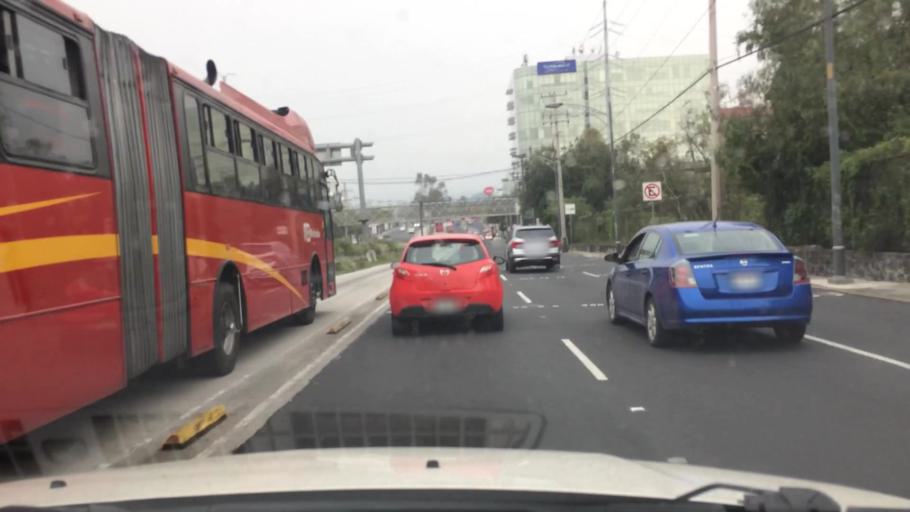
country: MX
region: Mexico City
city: Tlalpan
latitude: 19.3113
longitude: -99.1871
